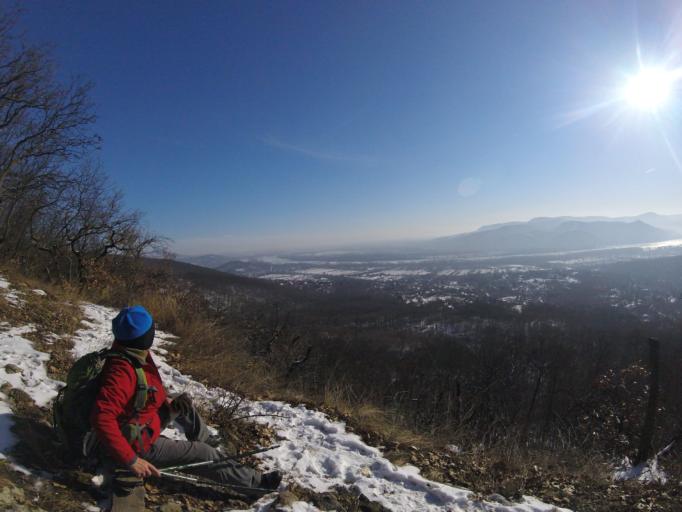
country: HU
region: Pest
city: Kismaros
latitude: 47.8358
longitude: 18.9806
